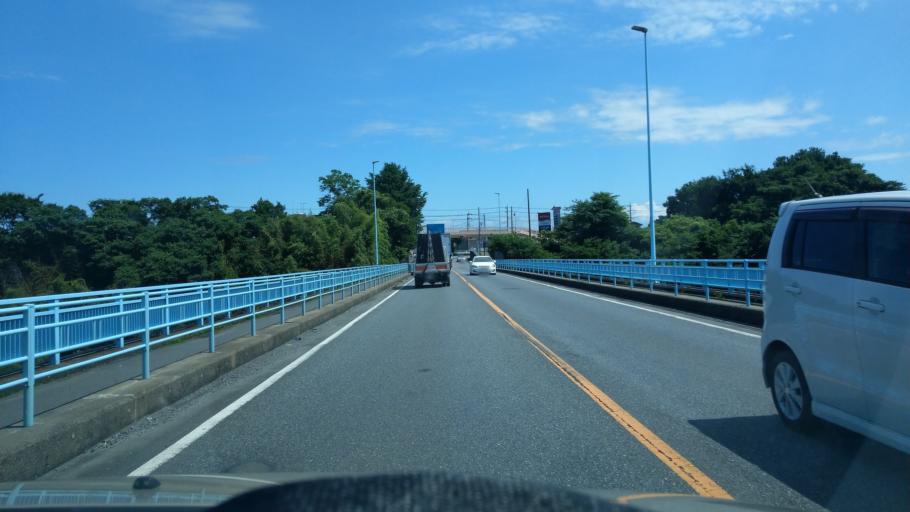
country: JP
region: Saitama
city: Yorii
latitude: 36.1204
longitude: 139.2117
